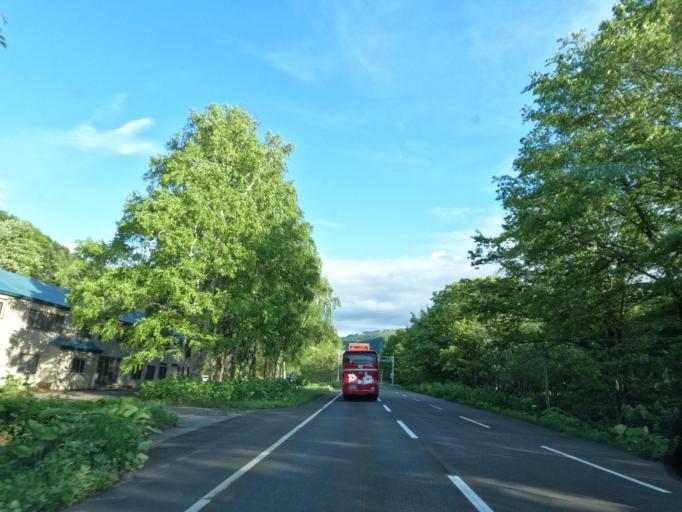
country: JP
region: Hokkaido
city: Kamikawa
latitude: 43.7828
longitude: 142.9018
